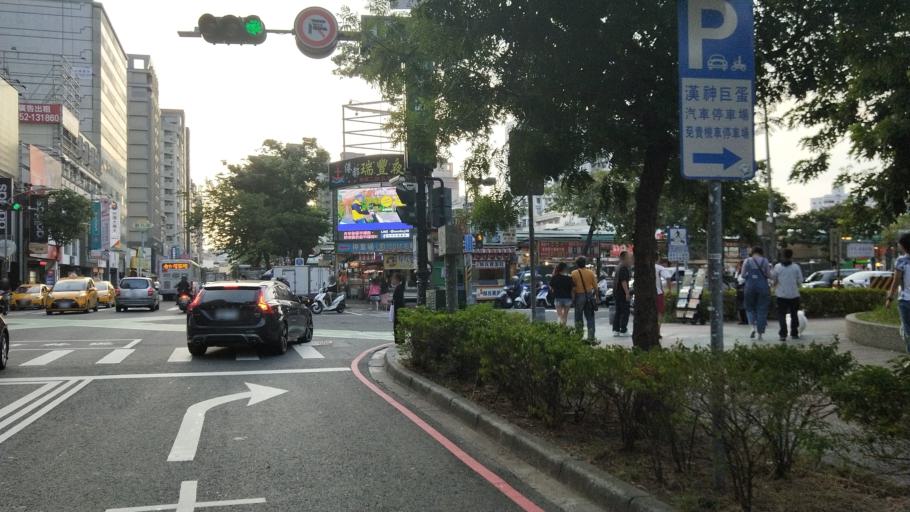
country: TW
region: Kaohsiung
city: Kaohsiung
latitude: 22.6659
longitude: 120.3004
